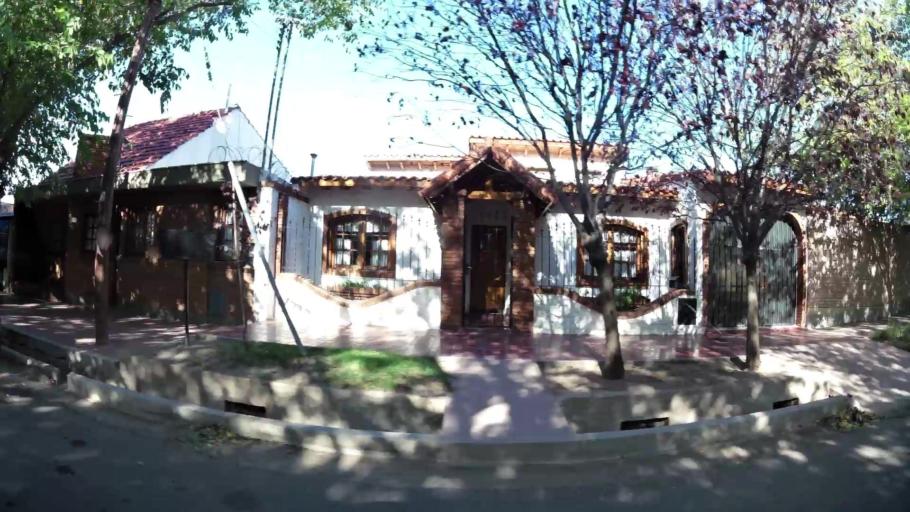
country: AR
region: Mendoza
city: Mendoza
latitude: -32.9088
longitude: -68.8240
